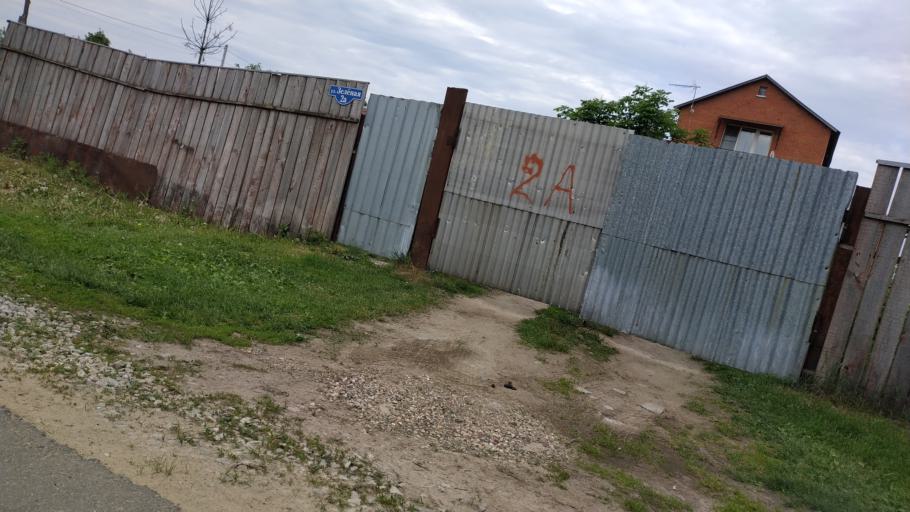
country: RU
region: Moskovskaya
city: Ostrovtsy
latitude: 55.5228
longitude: 37.9961
